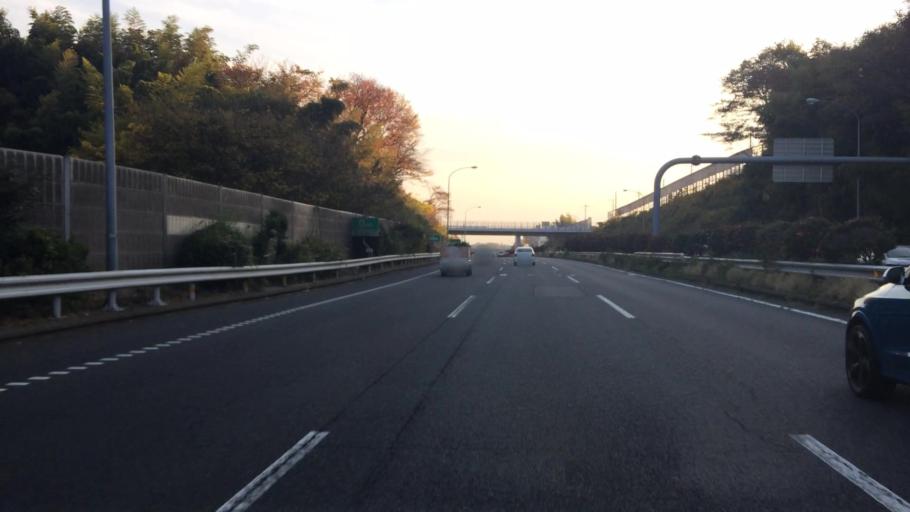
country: JP
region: Tokyo
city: Chofugaoka
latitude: 35.5810
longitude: 139.6179
